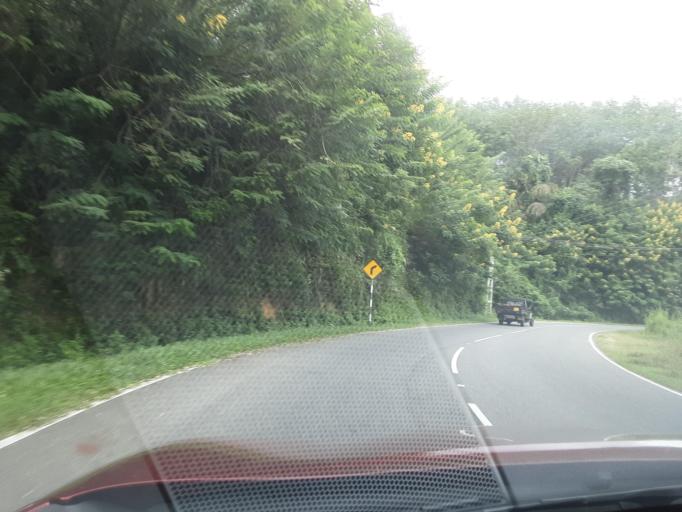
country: LK
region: Uva
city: Monaragala
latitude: 6.9006
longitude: 81.2128
